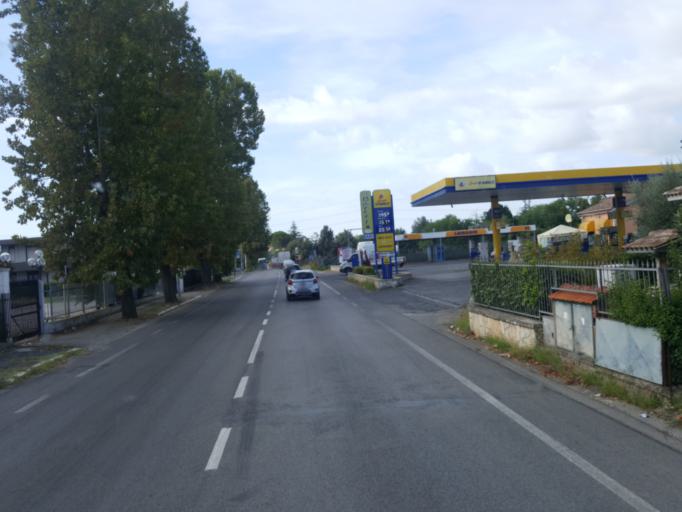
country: IT
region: Latium
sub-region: Citta metropolitana di Roma Capitale
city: Bivio di Capanelle
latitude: 42.1186
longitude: 12.5895
